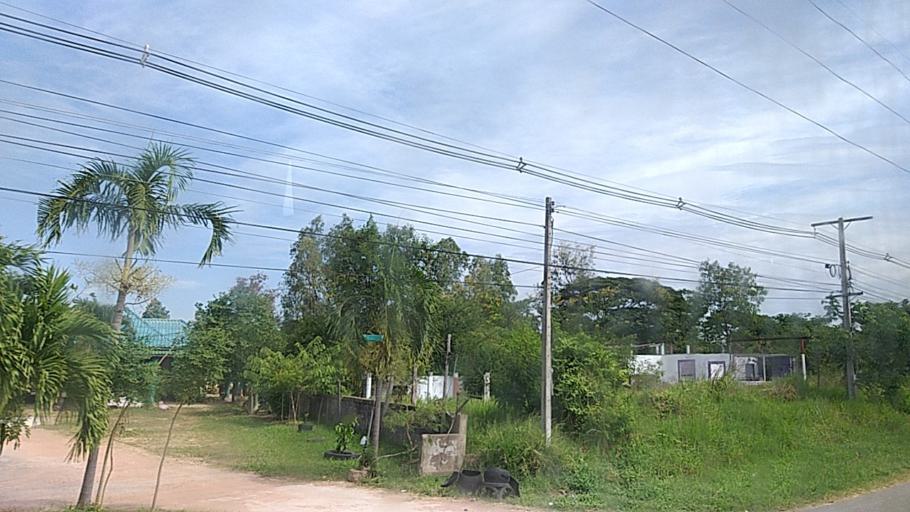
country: TH
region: Maha Sarakham
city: Chiang Yuen
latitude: 16.4457
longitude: 103.0289
